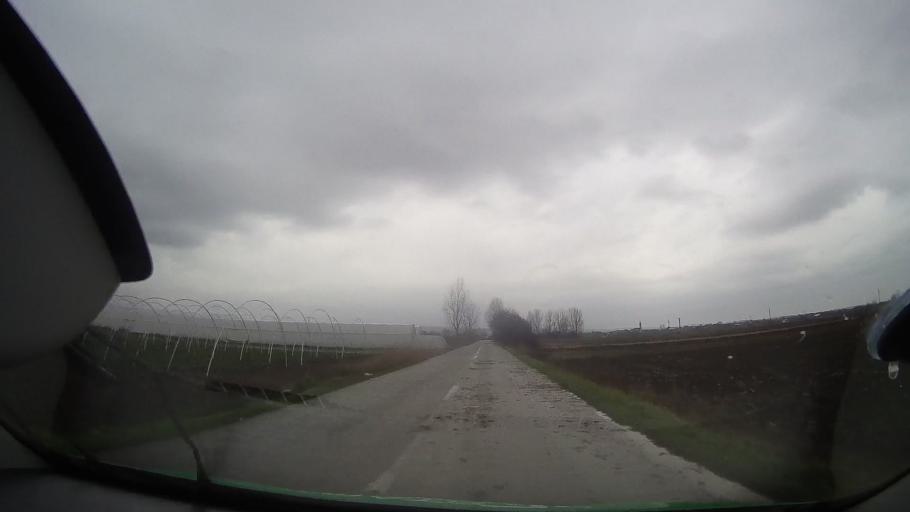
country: RO
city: Capalna
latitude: 46.7231
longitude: 22.0870
